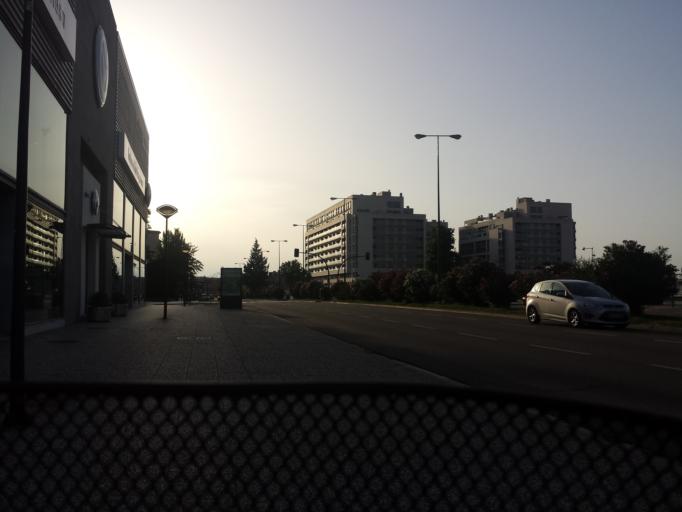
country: ES
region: Aragon
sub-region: Provincia de Zaragoza
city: Delicias
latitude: 41.6573
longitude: -0.9146
